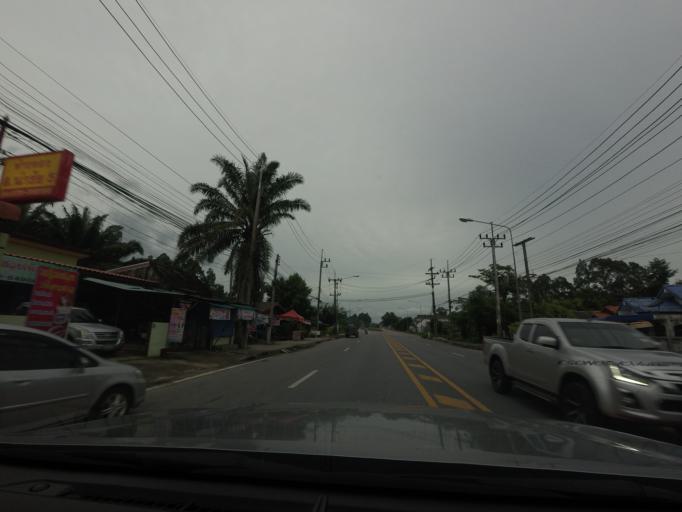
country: TH
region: Nakhon Si Thammarat
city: Chaloem Phra Kiat
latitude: 8.2503
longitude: 100.0125
